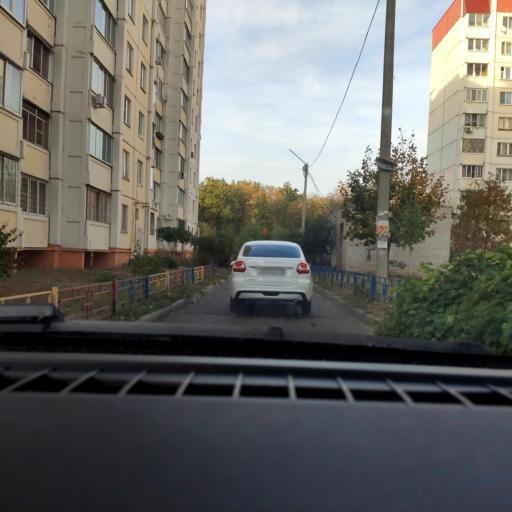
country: RU
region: Voronezj
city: Podgornoye
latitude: 51.7310
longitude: 39.2036
